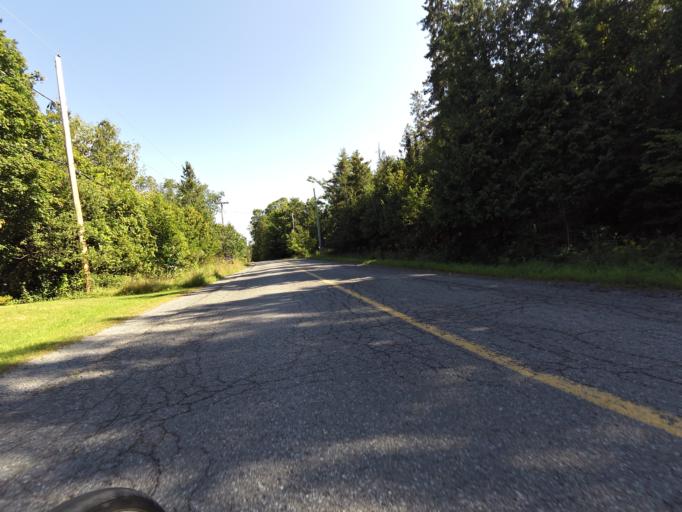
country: CA
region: Ontario
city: Bells Corners
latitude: 45.4647
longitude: -75.9750
